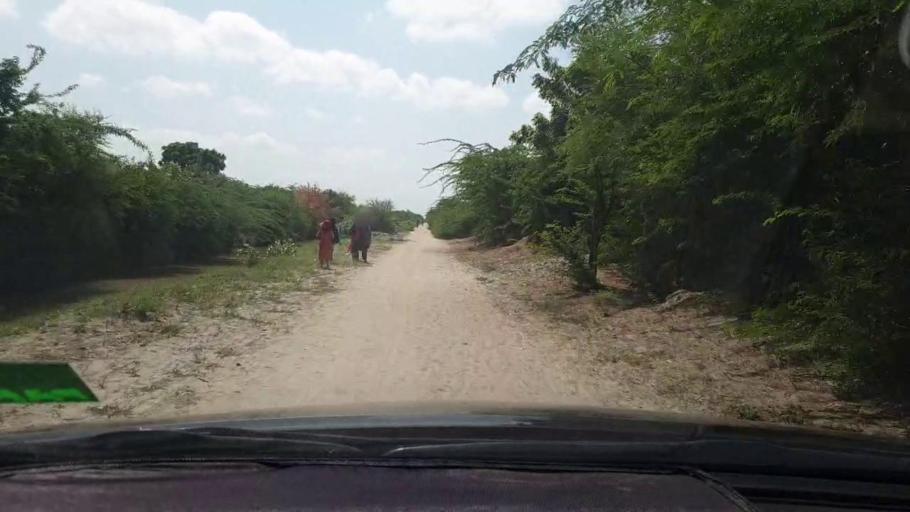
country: PK
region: Sindh
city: Tando Bago
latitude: 24.8738
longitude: 69.0709
